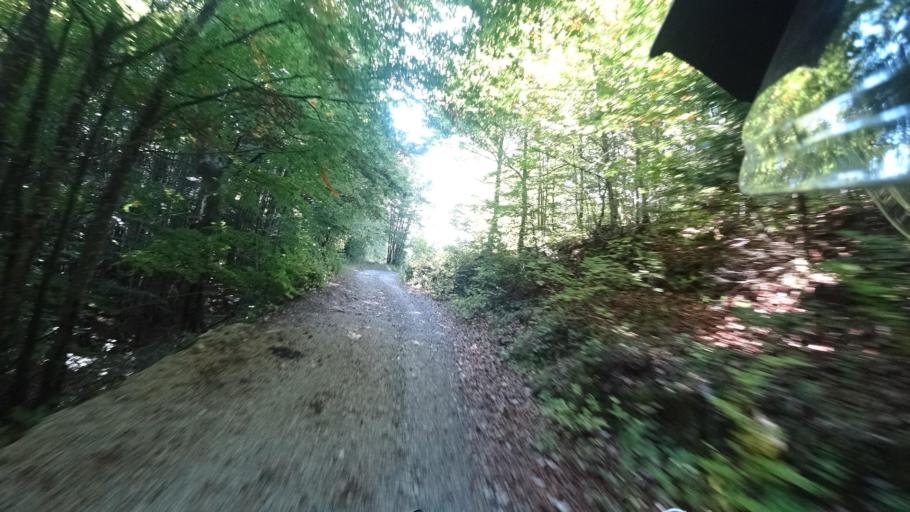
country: HR
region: Karlovacka
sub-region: Grad Ogulin
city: Ogulin
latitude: 45.1940
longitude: 15.1285
